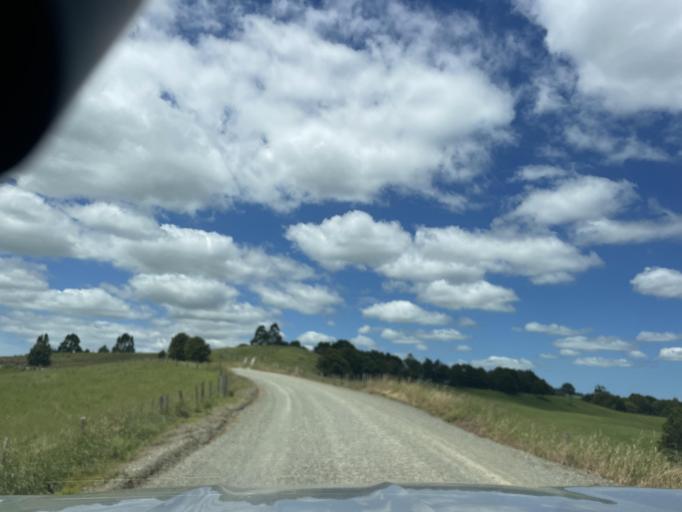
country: NZ
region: Auckland
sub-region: Auckland
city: Wellsford
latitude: -36.1607
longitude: 174.5302
